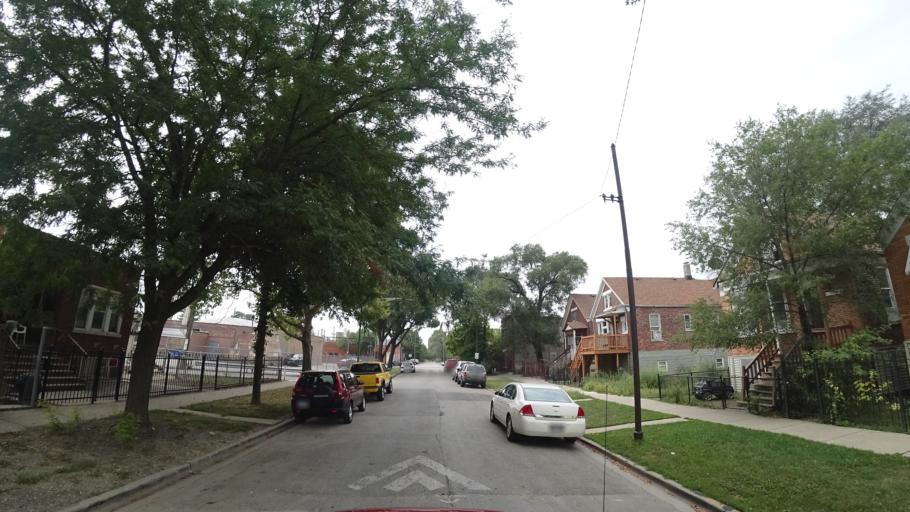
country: US
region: Illinois
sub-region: Cook County
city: Cicero
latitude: 41.8493
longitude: -87.7323
